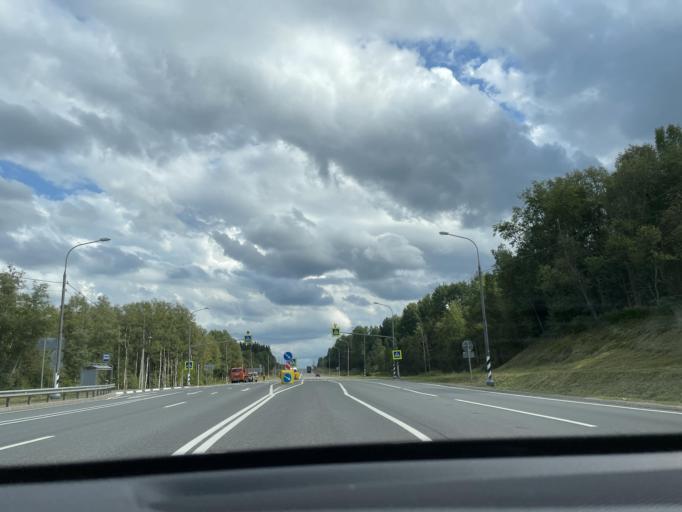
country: RU
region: Novgorod
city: Valday
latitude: 57.9980
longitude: 33.1613
